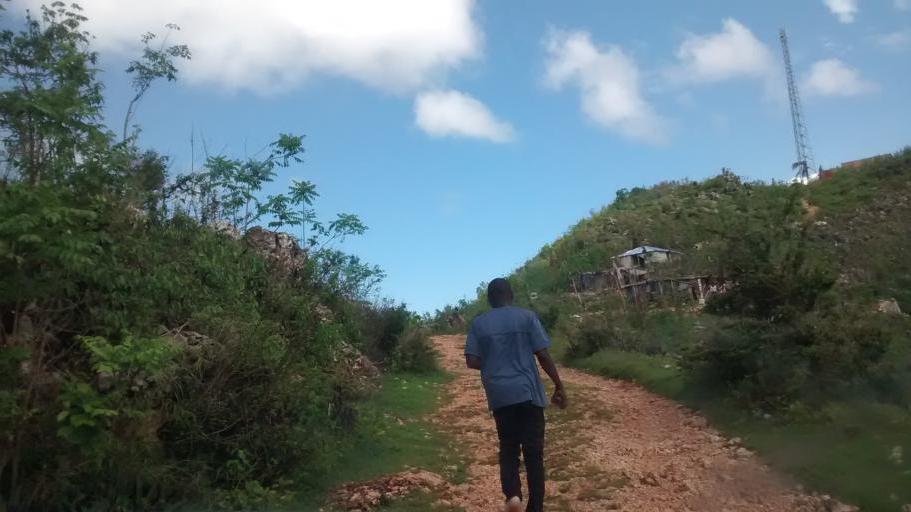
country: HT
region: Grandans
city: Corail
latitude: 18.5406
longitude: -73.9187
